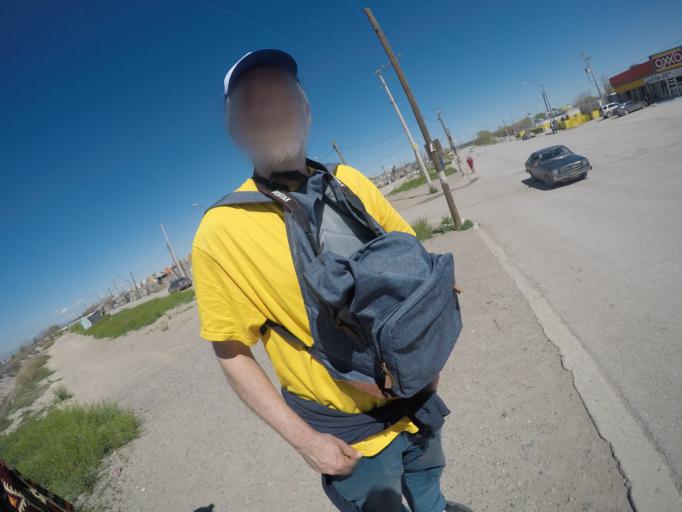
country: US
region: Texas
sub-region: El Paso County
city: Socorro Mission Number 1 Colonia
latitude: 31.6039
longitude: -106.3094
